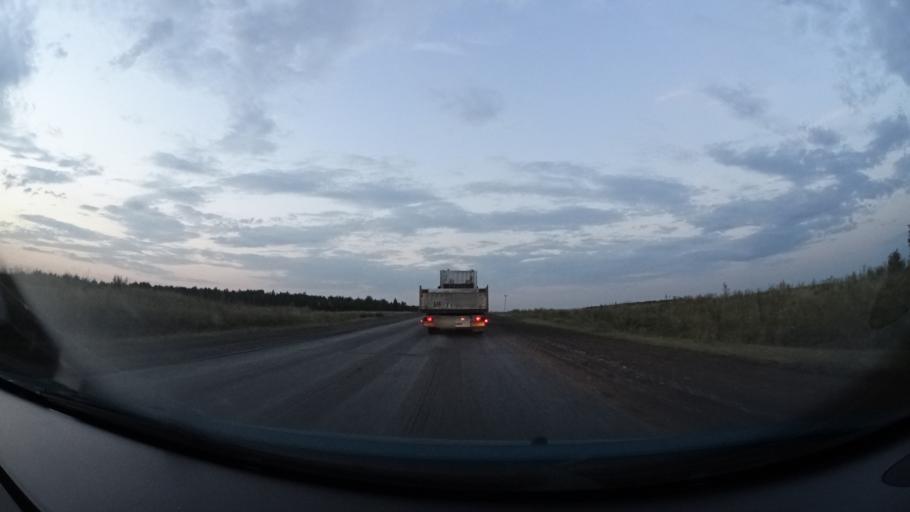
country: RU
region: Tatarstan
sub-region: Bavlinskiy Rayon
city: Bavly
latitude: 54.2967
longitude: 53.0079
